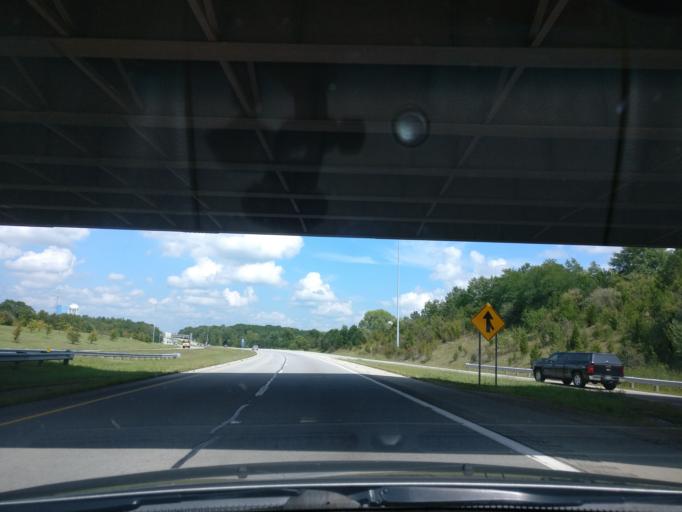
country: US
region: Ohio
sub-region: Greene County
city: Xenia
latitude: 39.6648
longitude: -83.9137
